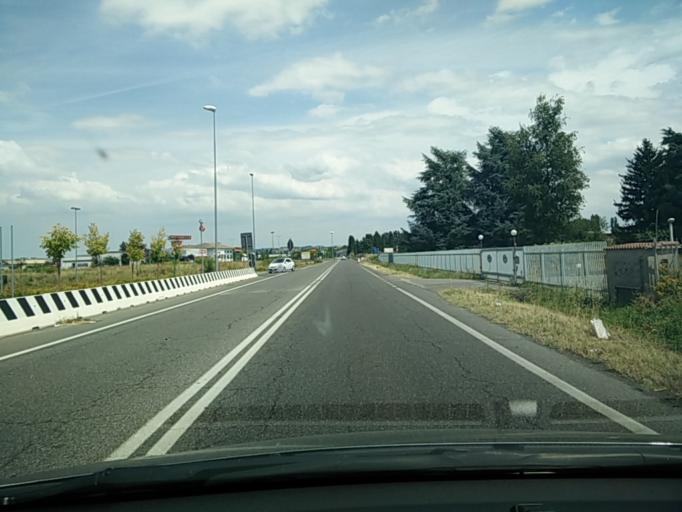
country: IT
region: Lombardy
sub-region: Provincia di Pavia
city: Torrazza Coste
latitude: 44.9970
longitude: 9.0633
